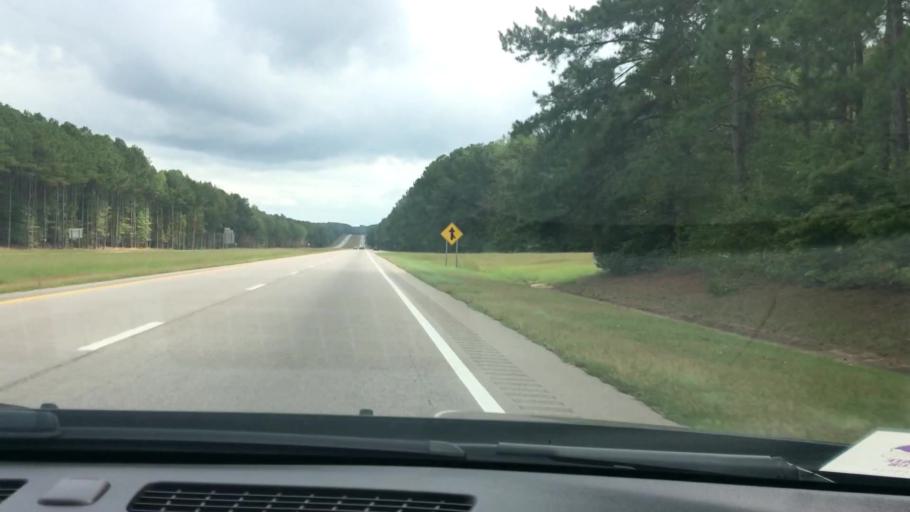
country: US
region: North Carolina
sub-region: Wake County
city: Zebulon
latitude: 35.8200
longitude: -78.2670
